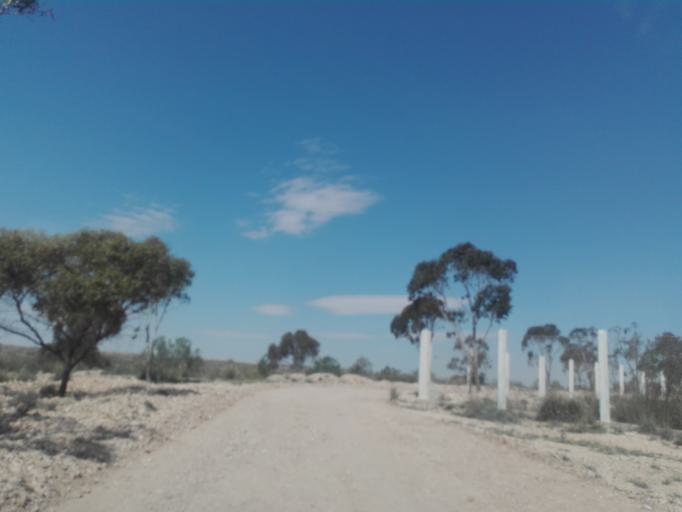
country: TN
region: Safaqis
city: Sfax
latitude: 34.7025
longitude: 10.5279
